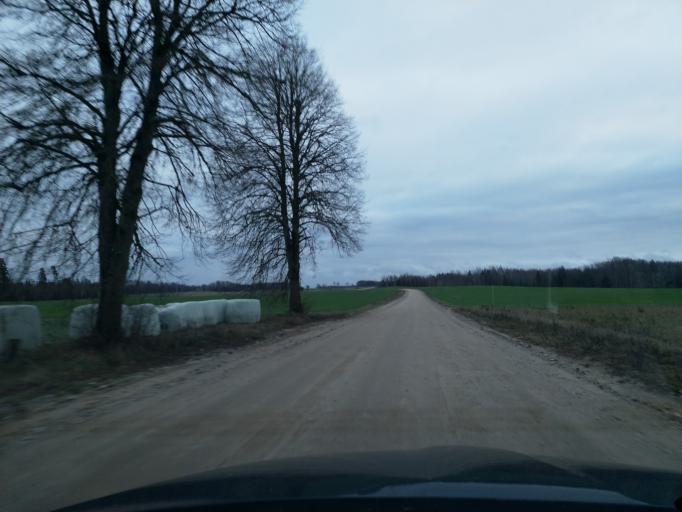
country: LV
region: Kuldigas Rajons
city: Kuldiga
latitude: 56.8944
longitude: 22.2601
